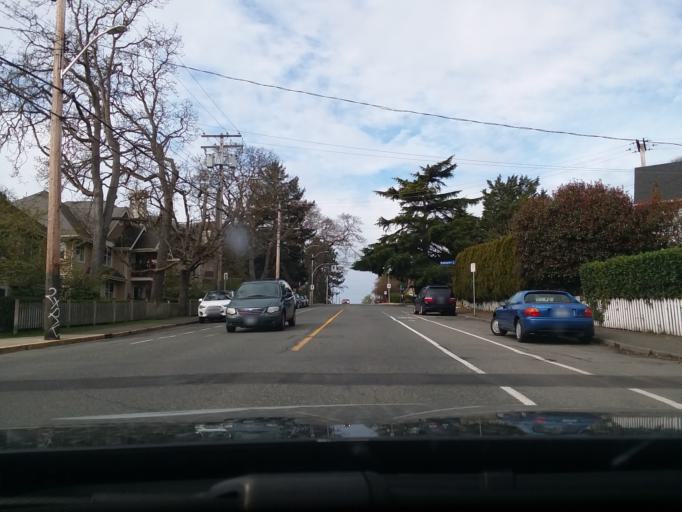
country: CA
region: British Columbia
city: Victoria
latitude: 48.4297
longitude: -123.3351
